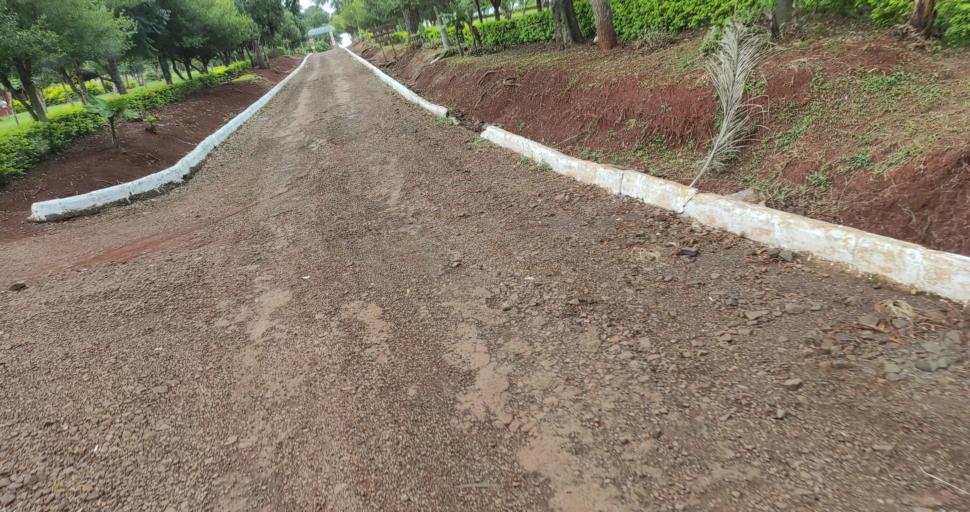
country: AR
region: Misiones
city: Puerto Libertad
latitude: -25.9578
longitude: -54.5973
